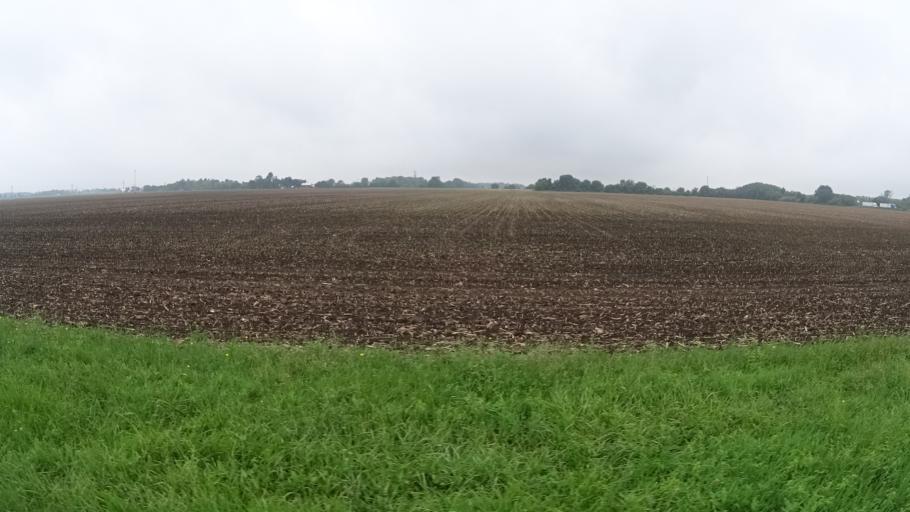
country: US
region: Ohio
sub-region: Huron County
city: Bellevue
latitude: 41.3455
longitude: -82.8167
